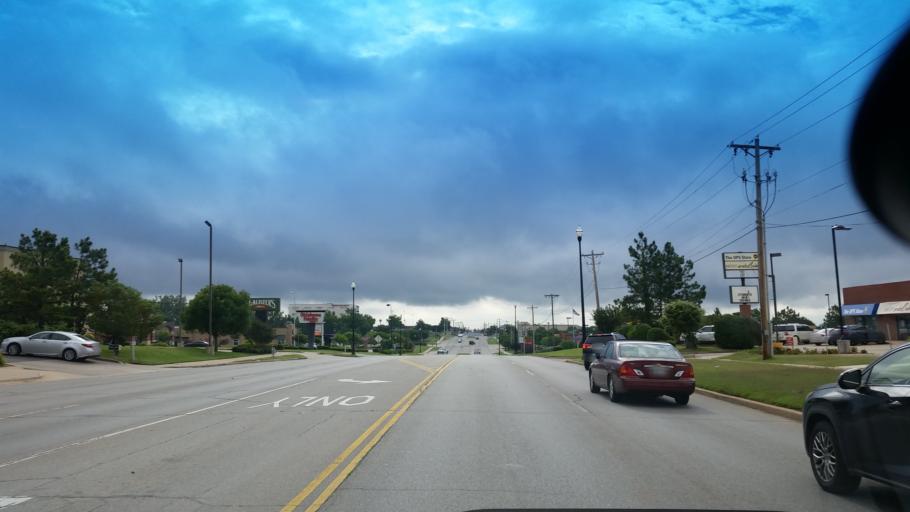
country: US
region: Oklahoma
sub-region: Oklahoma County
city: Edmond
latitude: 35.6527
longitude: -97.4669
